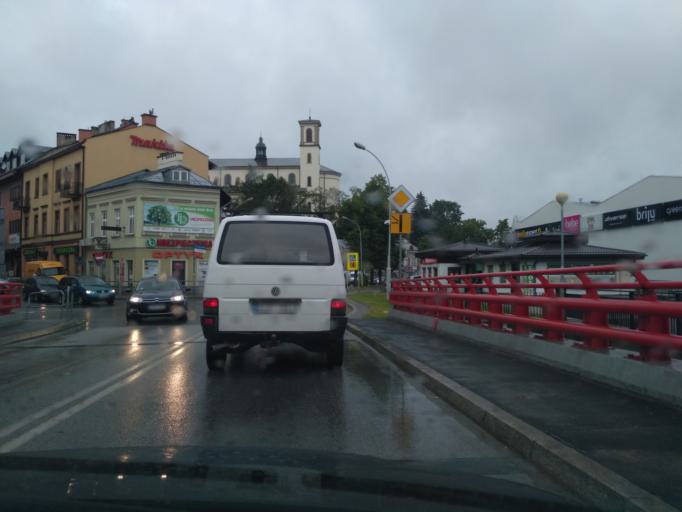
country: PL
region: Lesser Poland Voivodeship
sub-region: Powiat gorlicki
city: Gorlice
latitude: 49.6561
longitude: 21.1592
